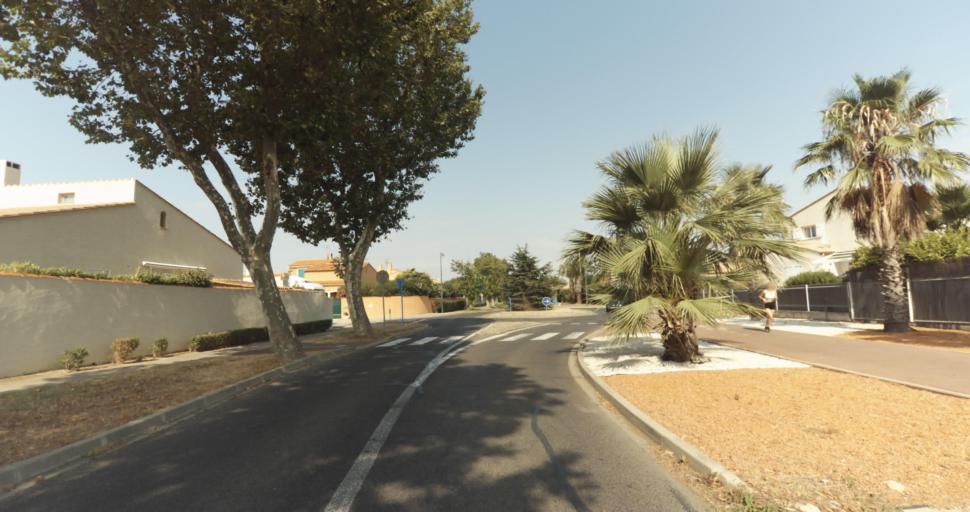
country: FR
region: Languedoc-Roussillon
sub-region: Departement des Pyrenees-Orientales
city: Latour-Bas-Elne
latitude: 42.6185
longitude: 3.0150
